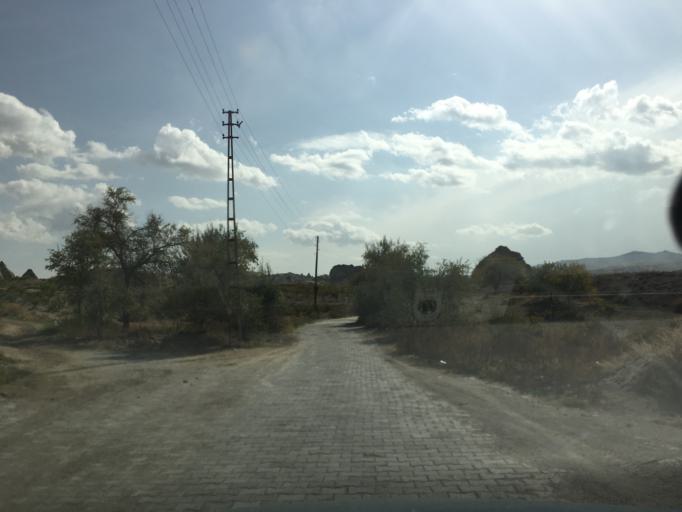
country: TR
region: Nevsehir
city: Goereme
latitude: 38.6649
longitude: 34.8412
